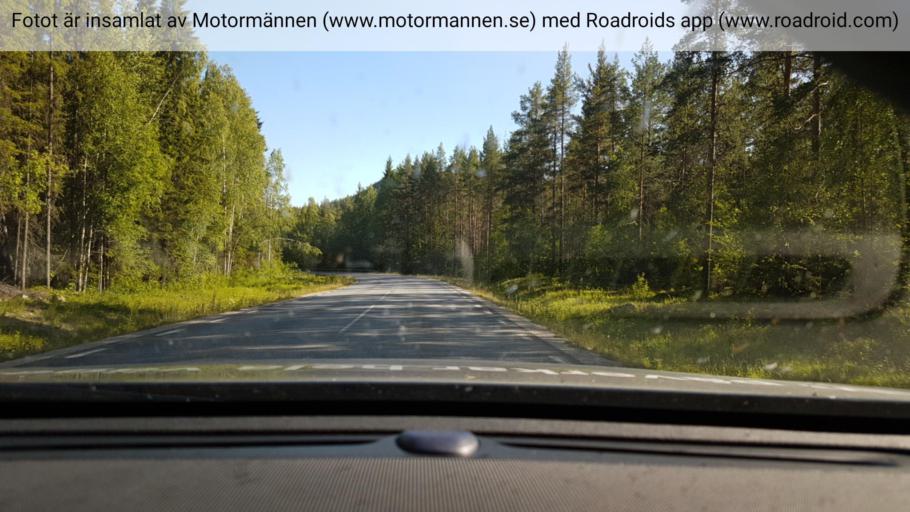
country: SE
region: Vaesterbotten
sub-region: Lycksele Kommun
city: Lycksele
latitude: 64.4217
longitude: 19.0037
